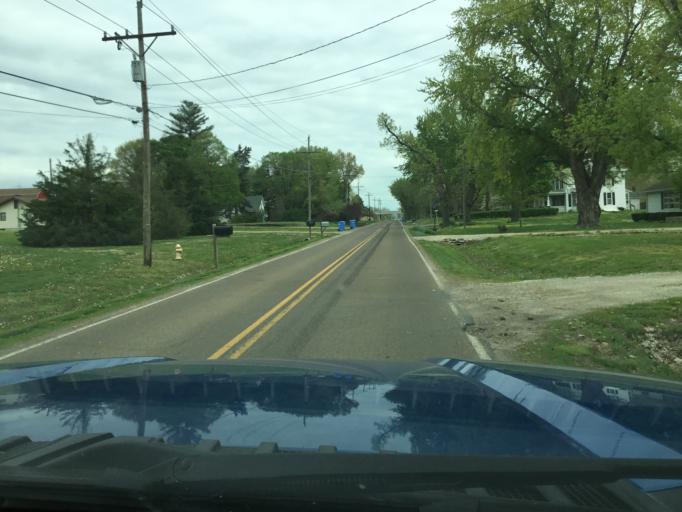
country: US
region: Kansas
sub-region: Douglas County
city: Lawrence
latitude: 38.9899
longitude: -95.2239
